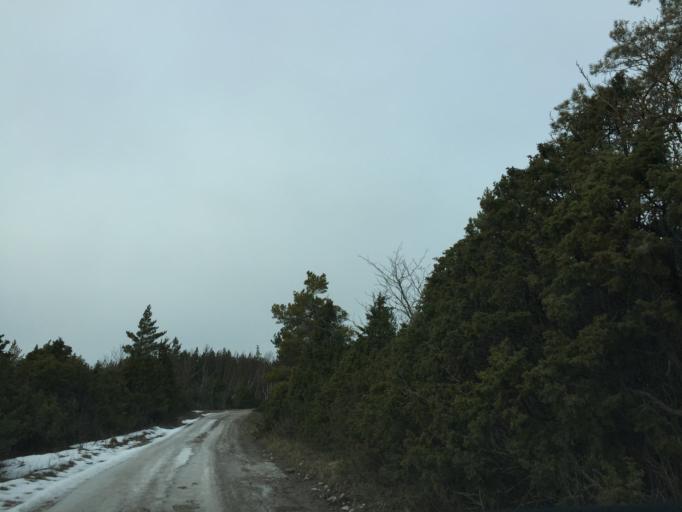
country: EE
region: Saare
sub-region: Kuressaare linn
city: Kuressaare
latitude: 58.4973
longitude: 21.9268
